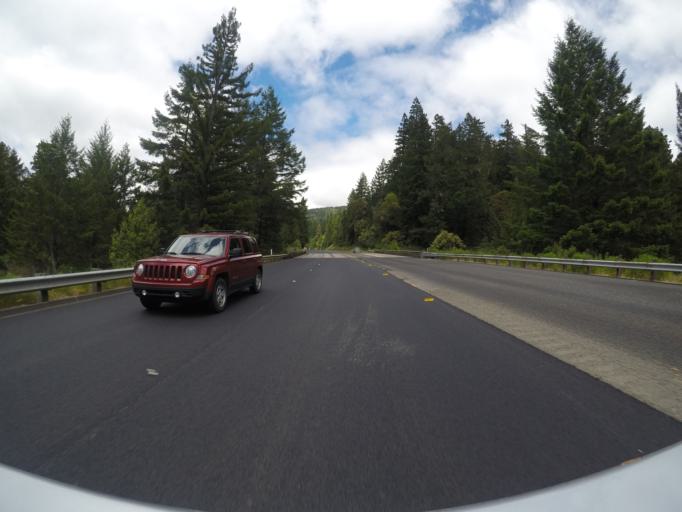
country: US
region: California
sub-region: Humboldt County
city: Redway
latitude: 40.2937
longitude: -123.8940
